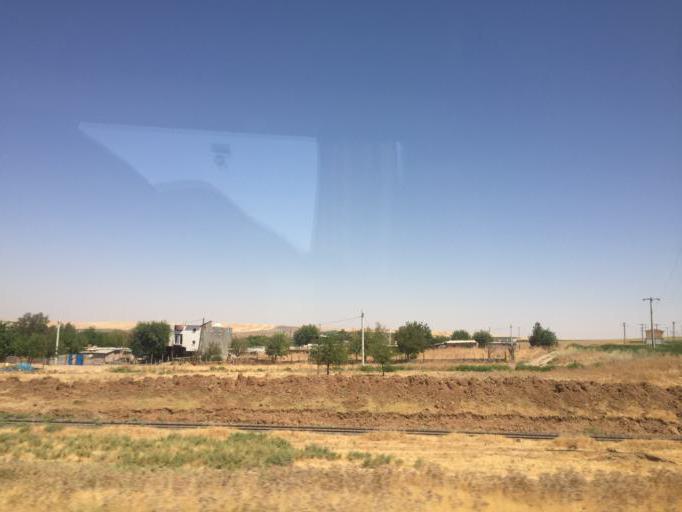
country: TR
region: Diyarbakir
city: Tepe
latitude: 37.8474
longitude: 40.8067
